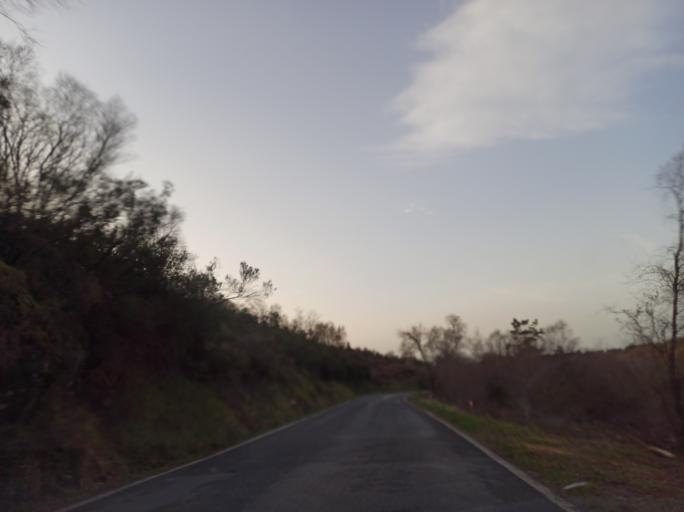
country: ES
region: Galicia
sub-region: Provincia da Coruna
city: Sobrado
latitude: 43.0348
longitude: -7.9419
